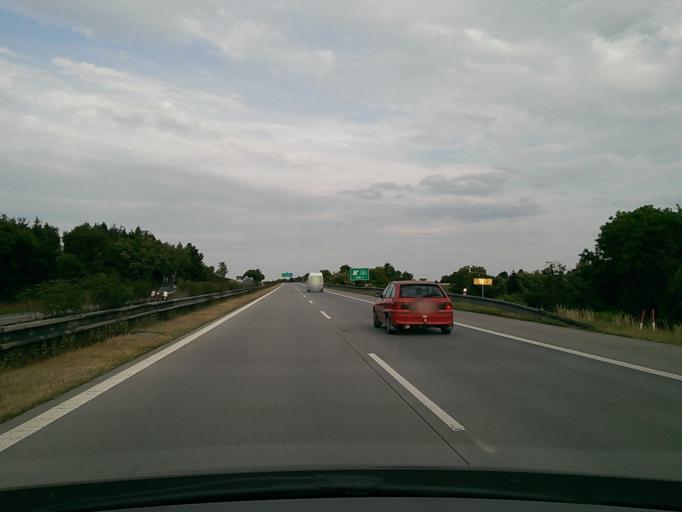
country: CZ
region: Vysocina
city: Merin
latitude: 49.3998
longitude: 15.8644
